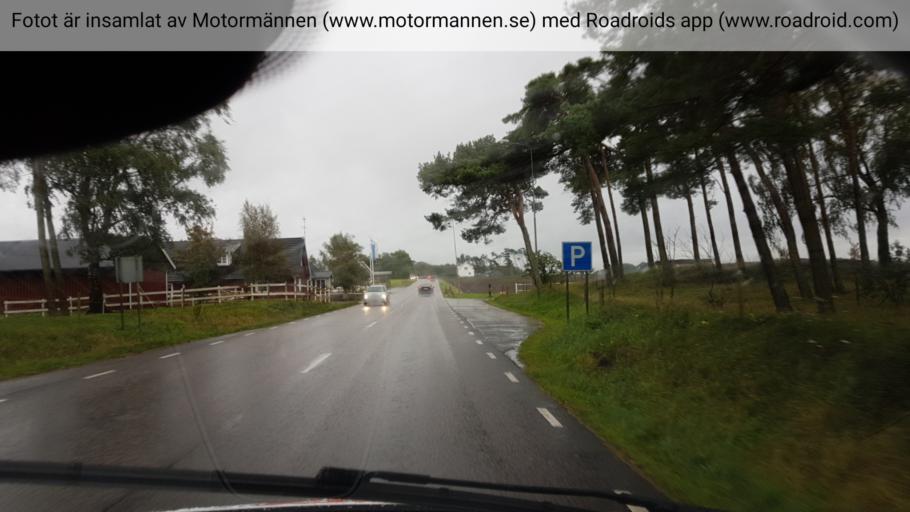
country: SE
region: Halland
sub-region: Laholms Kommun
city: Laholm
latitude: 56.4900
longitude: 13.0380
